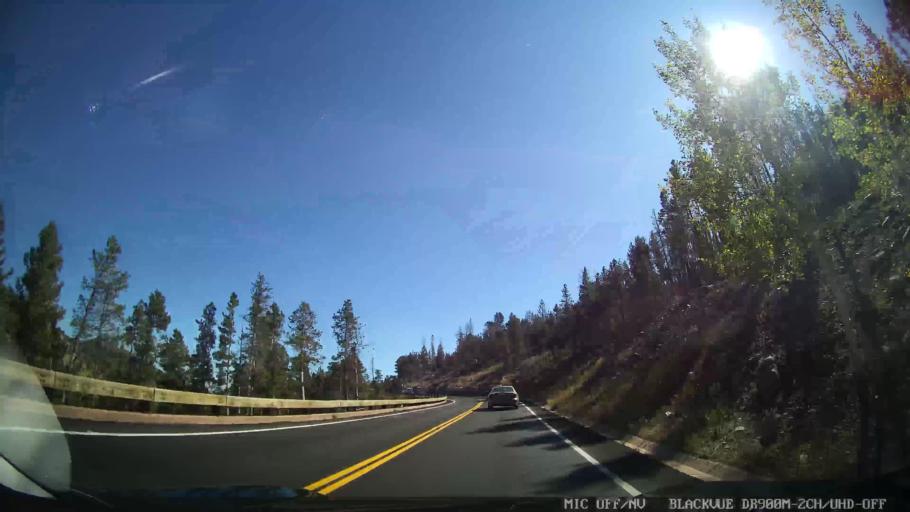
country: US
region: Colorado
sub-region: Larimer County
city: Estes Park
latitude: 40.3415
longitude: -105.5989
